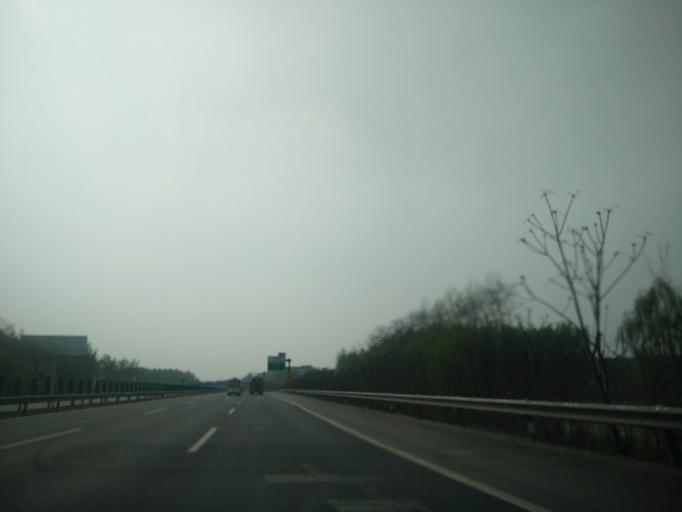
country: CN
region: Beijing
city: Xiji
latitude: 39.8030
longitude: 116.8446
